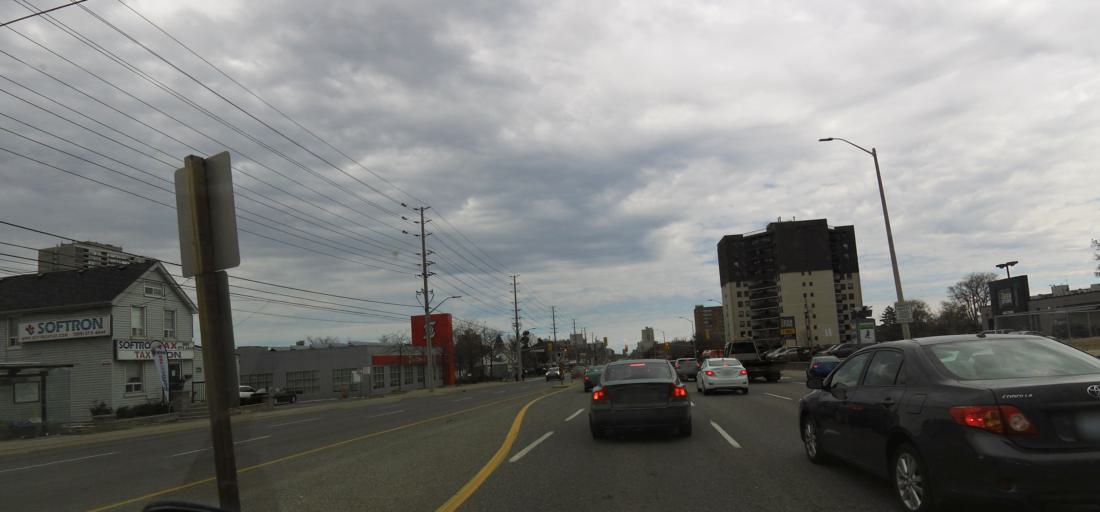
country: CA
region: Ontario
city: Mississauga
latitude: 43.5836
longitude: -79.6212
